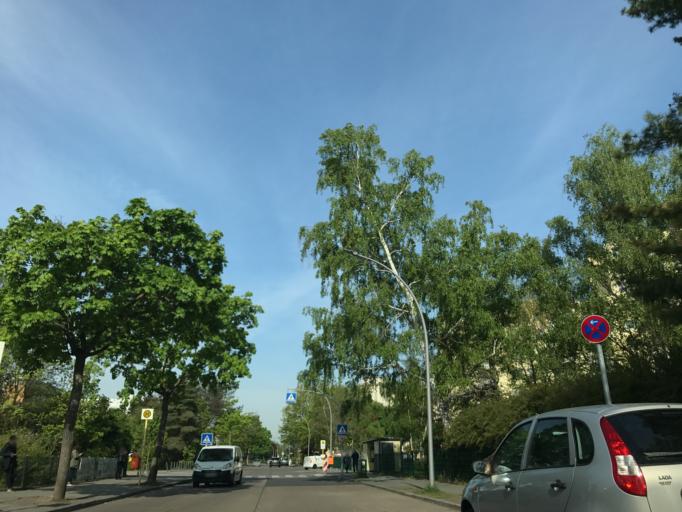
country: DE
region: Berlin
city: Falkenhagener Feld
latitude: 52.5489
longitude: 13.1572
